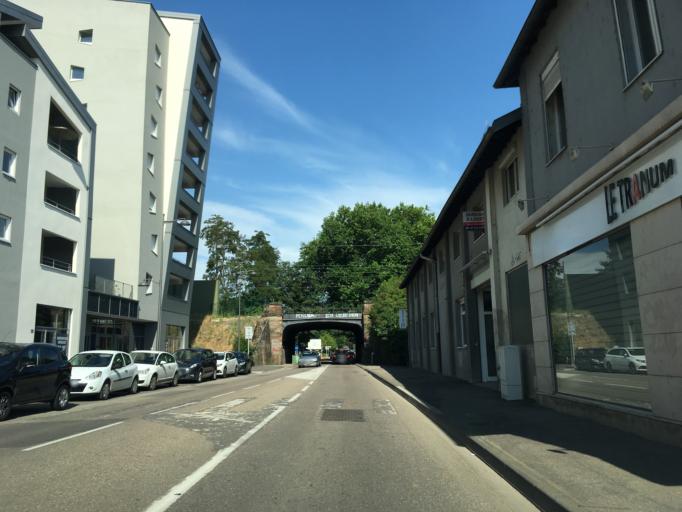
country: FR
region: Lorraine
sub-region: Departement de la Moselle
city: Metz
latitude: 49.1004
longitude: 6.1828
